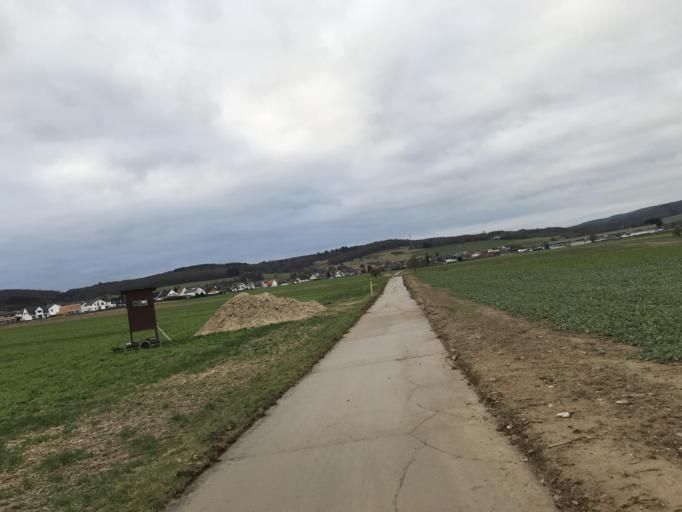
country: DE
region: Hesse
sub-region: Regierungsbezirk Darmstadt
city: Butzbach
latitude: 50.4560
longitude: 8.6213
